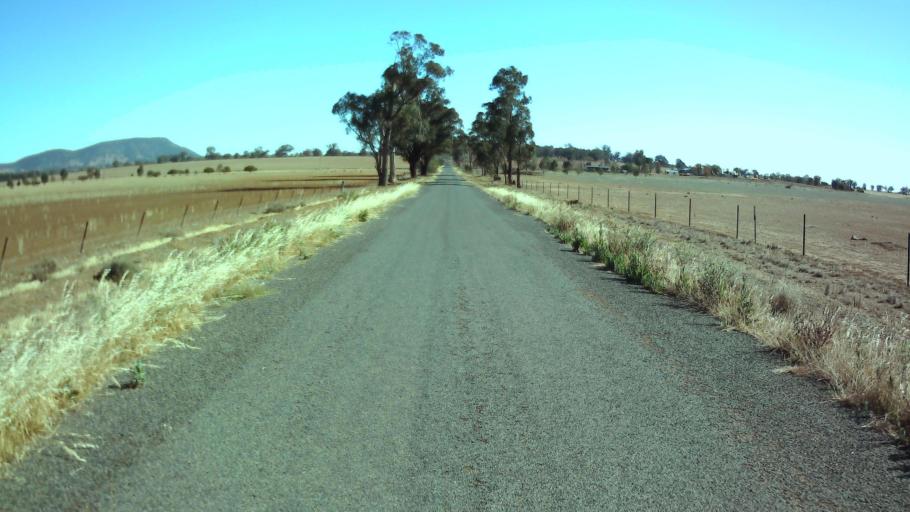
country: AU
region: New South Wales
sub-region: Weddin
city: Grenfell
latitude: -33.7966
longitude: 147.9565
